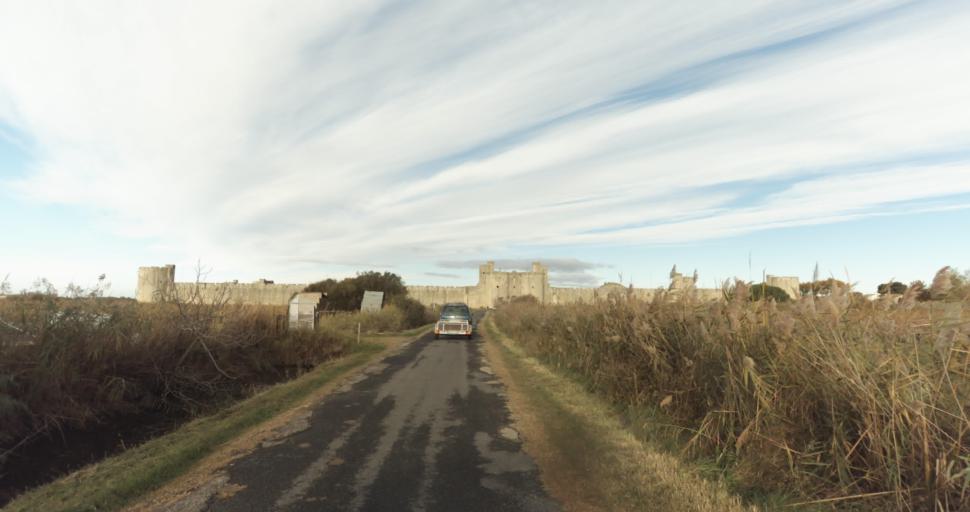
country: FR
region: Languedoc-Roussillon
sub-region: Departement du Gard
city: Aigues-Mortes
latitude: 43.5634
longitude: 4.1962
